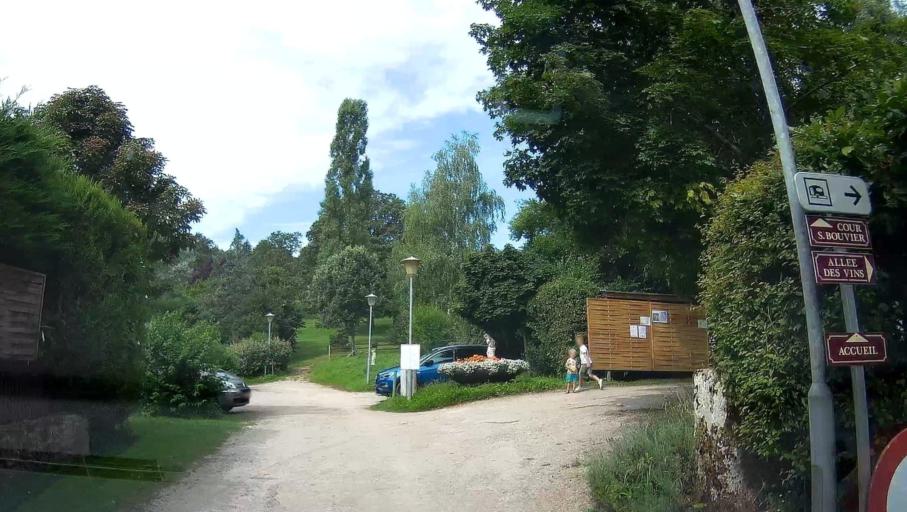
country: FR
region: Bourgogne
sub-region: Departement de Saone-et-Loire
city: Couches
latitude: 46.8688
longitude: 4.6052
